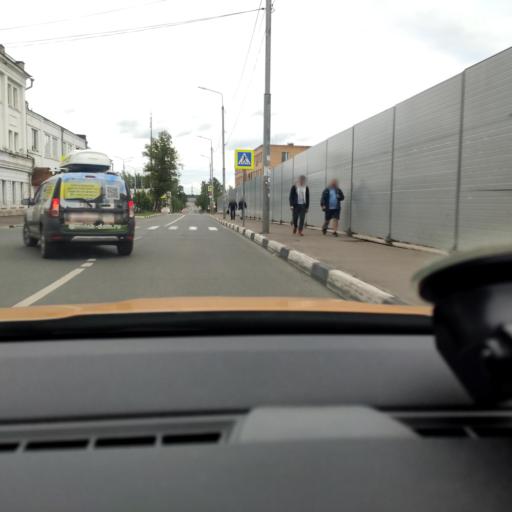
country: RU
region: Moskovskaya
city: Mytishchi
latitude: 55.9125
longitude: 37.7644
